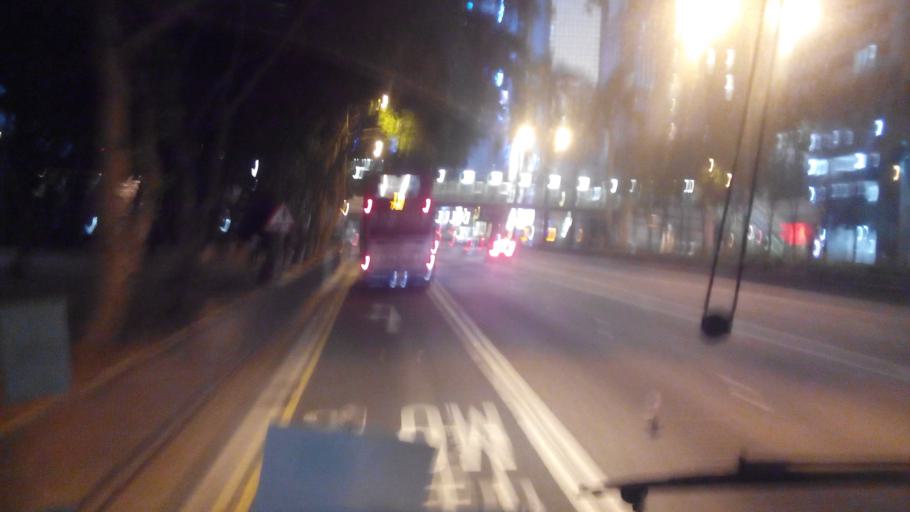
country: HK
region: Wanchai
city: Wan Chai
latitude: 22.2795
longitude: 114.1736
